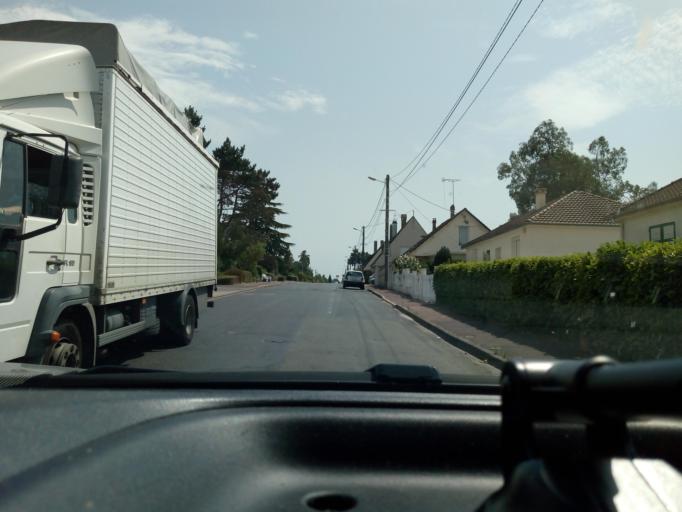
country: FR
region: Haute-Normandie
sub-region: Departement de la Seine-Maritime
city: Le Petit-Quevilly
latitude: 49.4039
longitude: 1.0588
